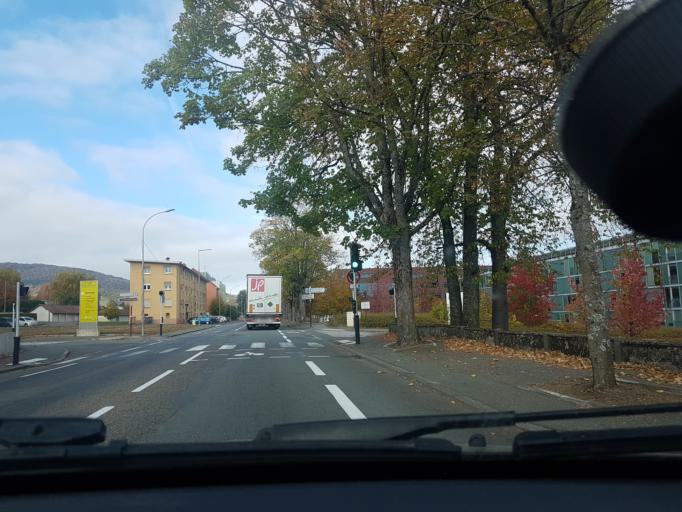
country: FR
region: Franche-Comte
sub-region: Territoire de Belfort
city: Cravanche
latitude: 47.6437
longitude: 6.8409
